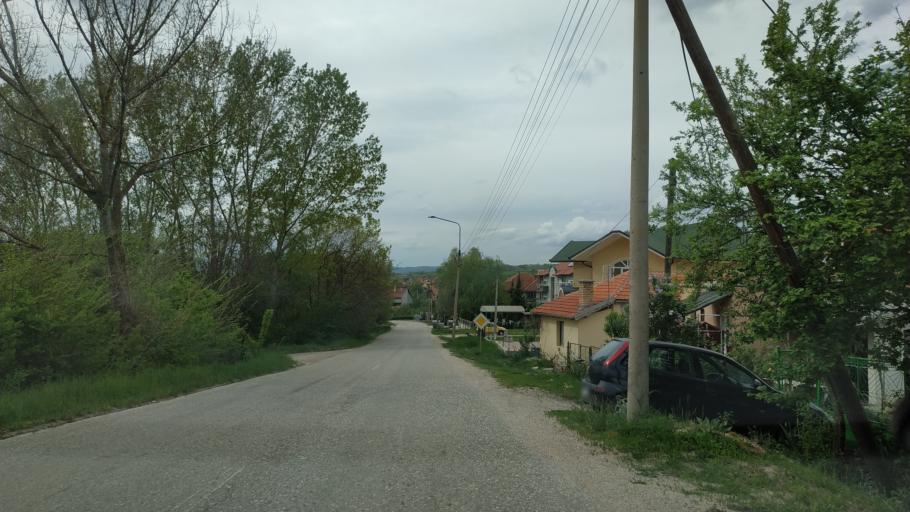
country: RS
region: Central Serbia
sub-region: Zajecarski Okrug
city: Soko Banja
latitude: 43.6442
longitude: 21.8873
